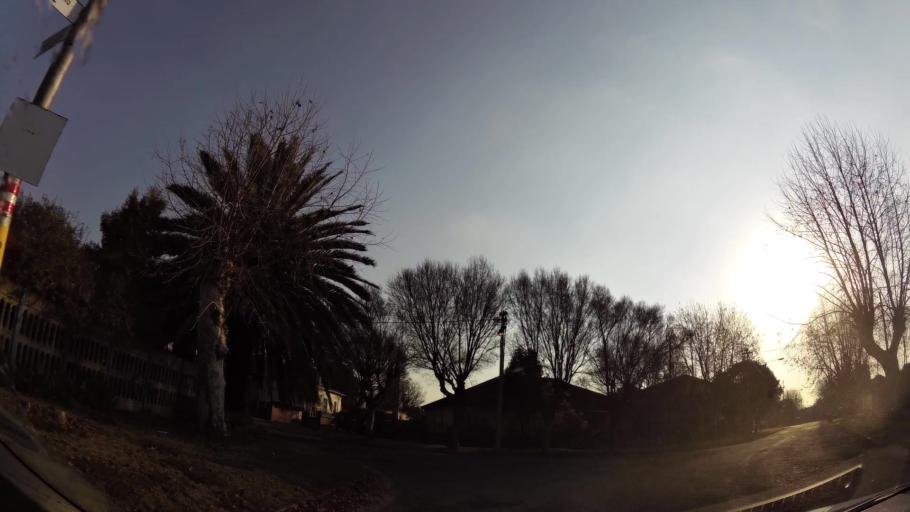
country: ZA
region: Gauteng
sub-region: Ekurhuleni Metropolitan Municipality
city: Springs
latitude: -26.2918
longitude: 28.4445
